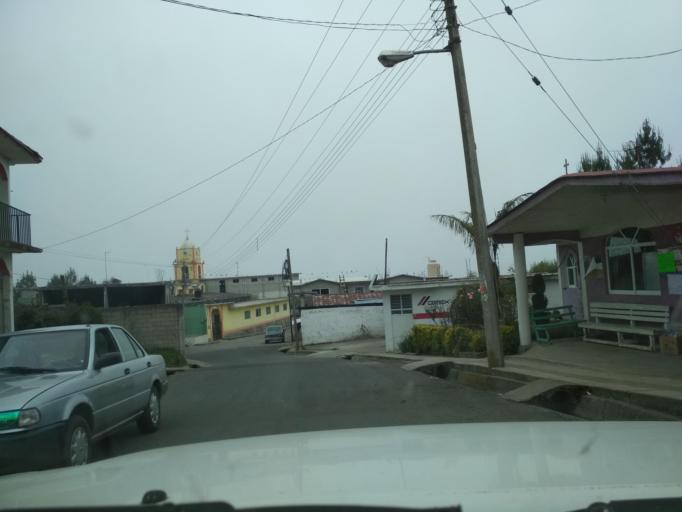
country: MX
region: Veracruz
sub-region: La Perla
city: Chilapa
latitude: 18.9756
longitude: -97.1892
